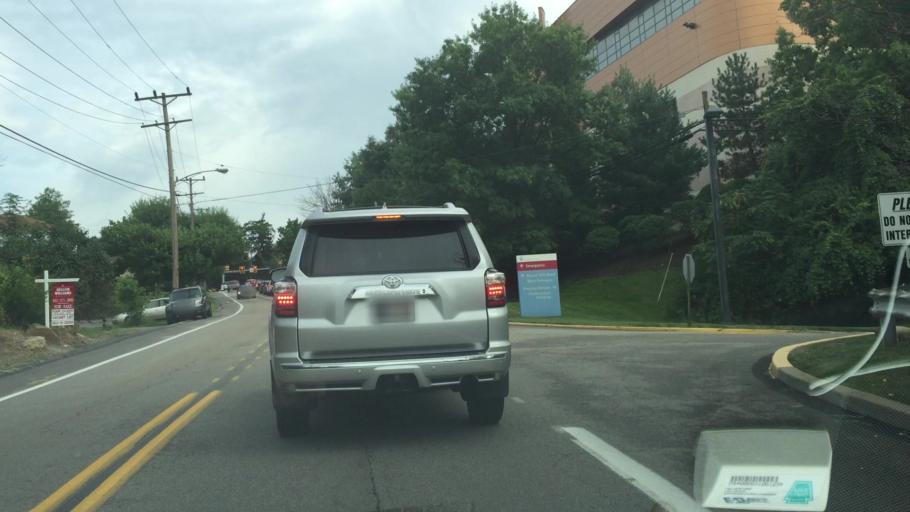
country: US
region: Pennsylvania
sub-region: Allegheny County
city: Heidelberg
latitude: 40.3798
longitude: -80.0662
